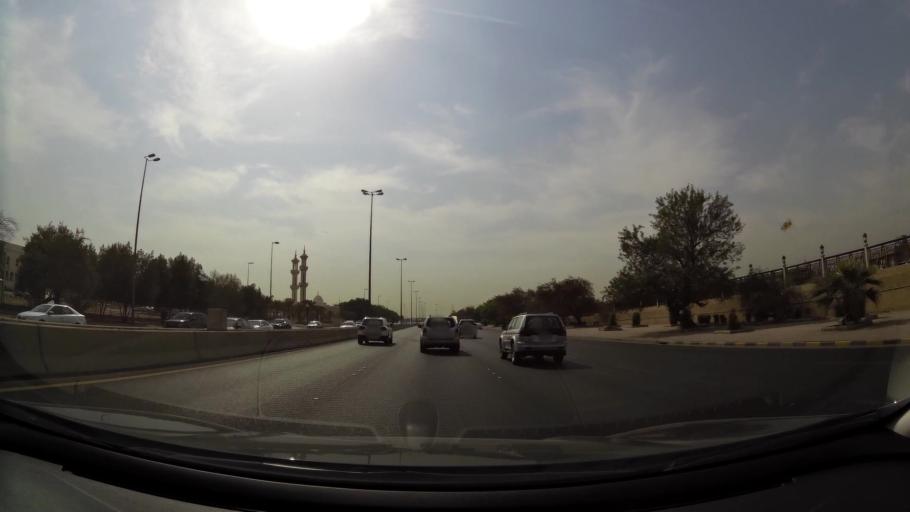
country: KW
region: Al Asimah
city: Ash Shamiyah
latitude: 29.3256
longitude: 47.9727
